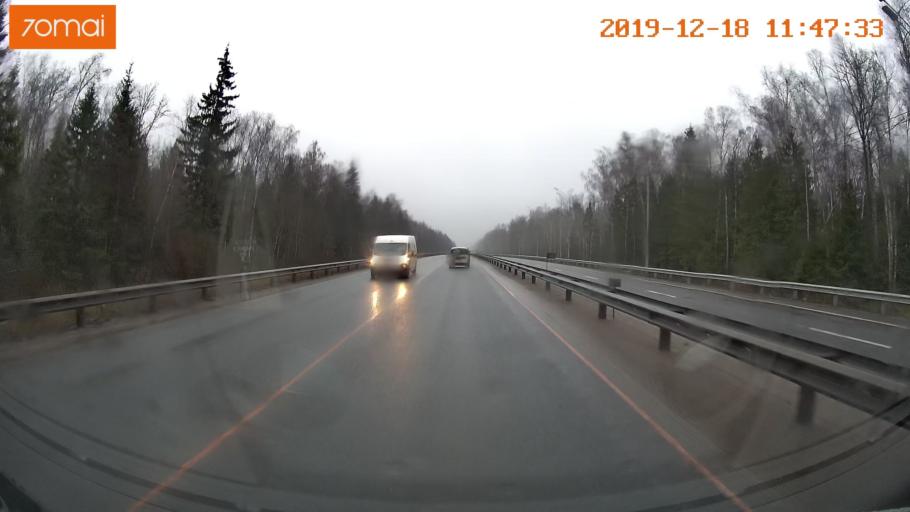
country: RU
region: Moskovskaya
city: Yershovo
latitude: 55.7589
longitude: 36.8956
